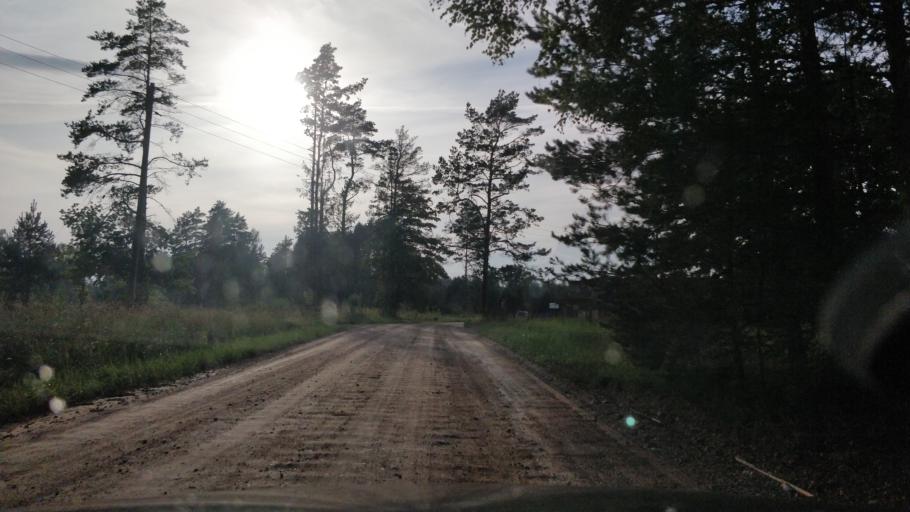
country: LV
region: Incukalns
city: Incukalns
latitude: 57.0940
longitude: 24.7624
